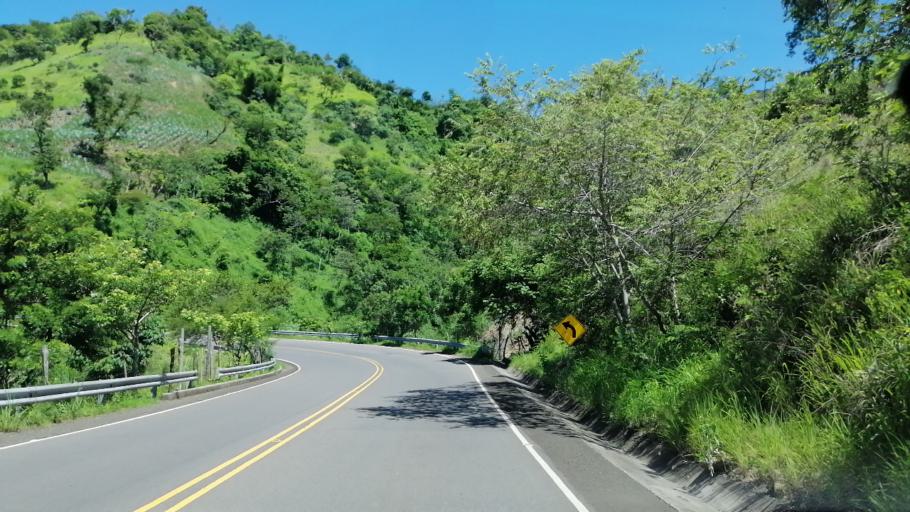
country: SV
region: San Miguel
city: Ciudad Barrios
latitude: 13.8127
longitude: -88.1781
